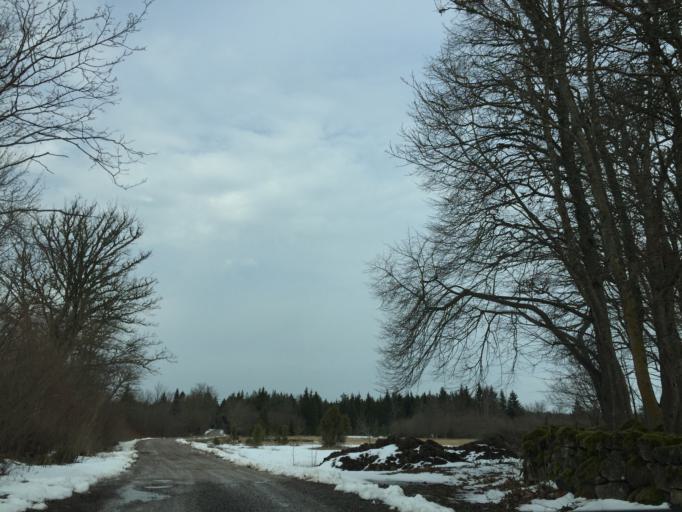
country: EE
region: Saare
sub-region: Kuressaare linn
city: Kuressaare
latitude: 58.4220
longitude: 22.1513
